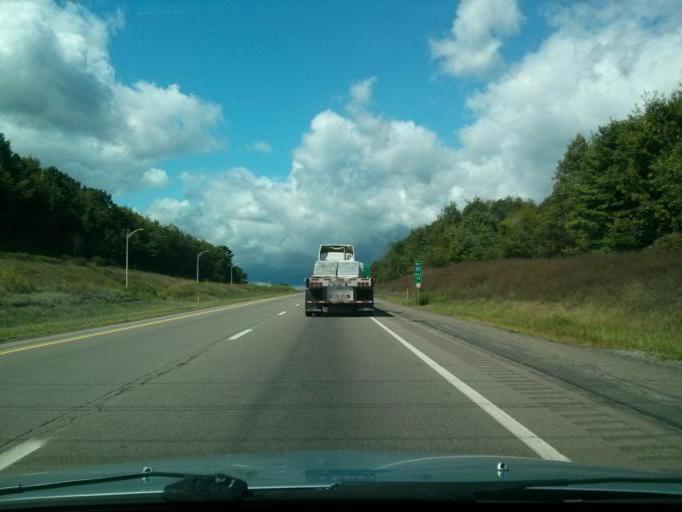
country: US
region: Pennsylvania
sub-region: Jefferson County
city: Brookville
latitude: 41.1706
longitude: -79.0892
